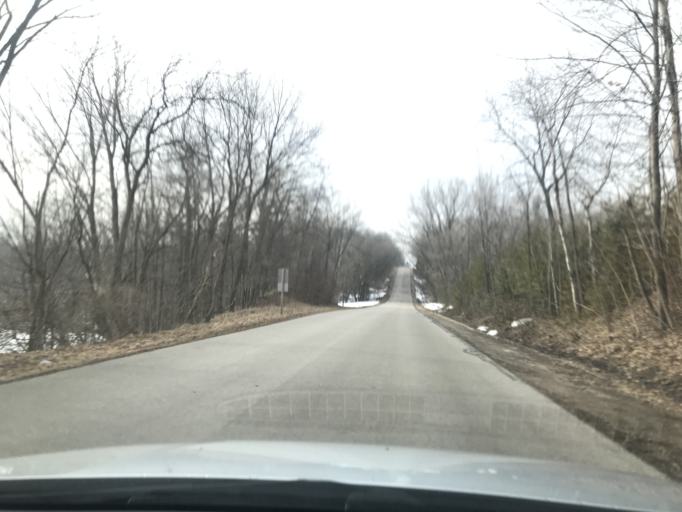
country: US
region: Wisconsin
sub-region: Oconto County
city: Oconto Falls
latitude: 44.8663
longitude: -88.1466
